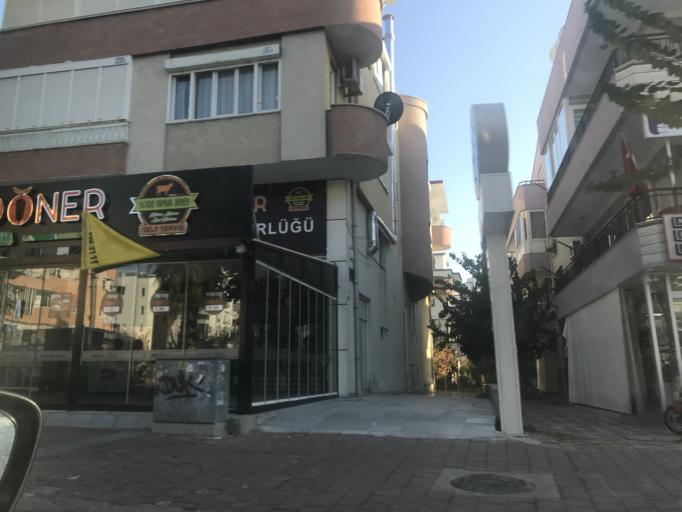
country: TR
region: Antalya
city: Antalya
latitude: 36.8538
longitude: 30.7760
